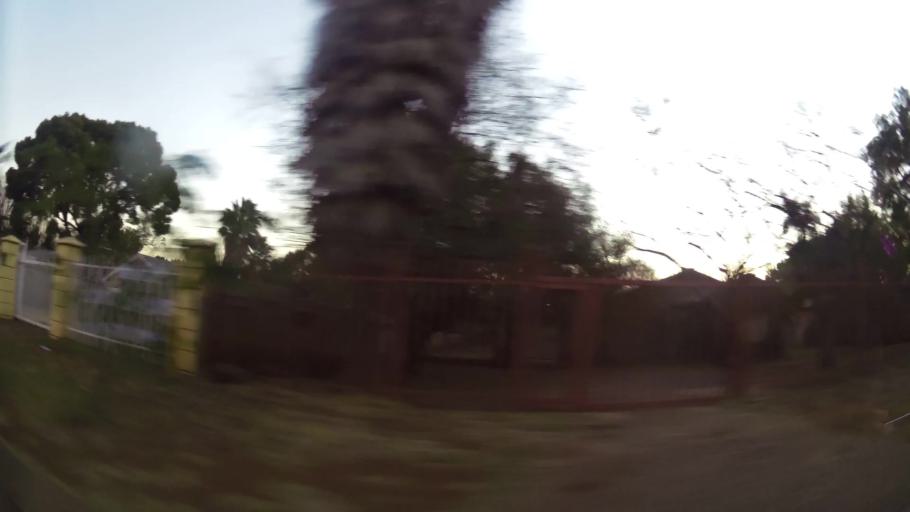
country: ZA
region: Gauteng
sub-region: City of Tshwane Metropolitan Municipality
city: Centurion
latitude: -25.8569
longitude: 28.1341
